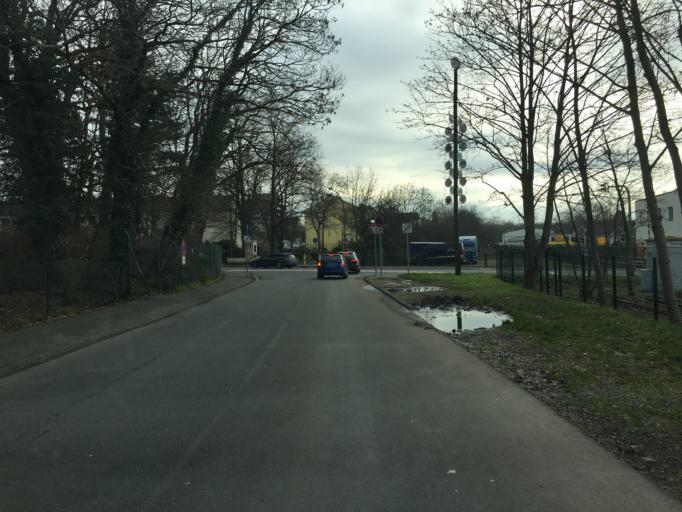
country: DE
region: North Rhine-Westphalia
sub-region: Regierungsbezirk Koln
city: Leverkusen
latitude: 51.0019
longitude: 6.9810
